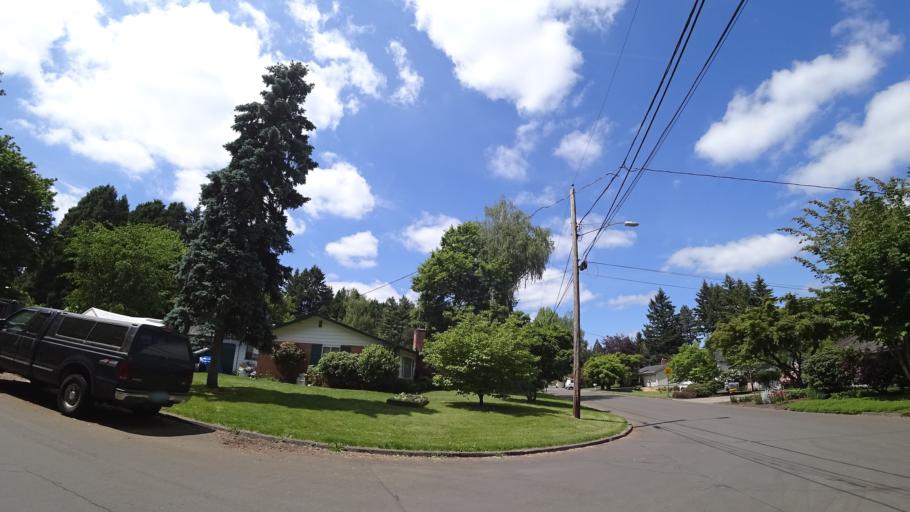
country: US
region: Oregon
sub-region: Washington County
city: Tigard
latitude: 45.4311
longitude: -122.7963
